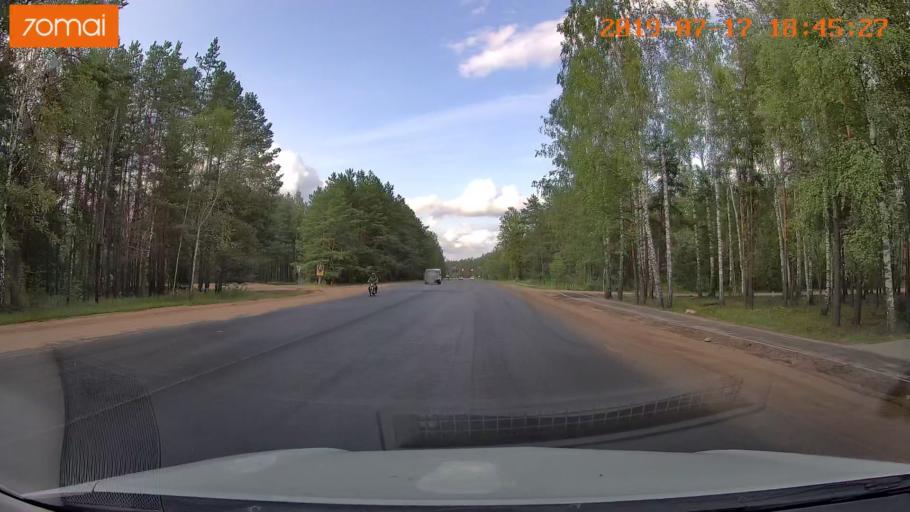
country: BY
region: Mogilev
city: Asipovichy
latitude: 53.3249
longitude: 28.6548
